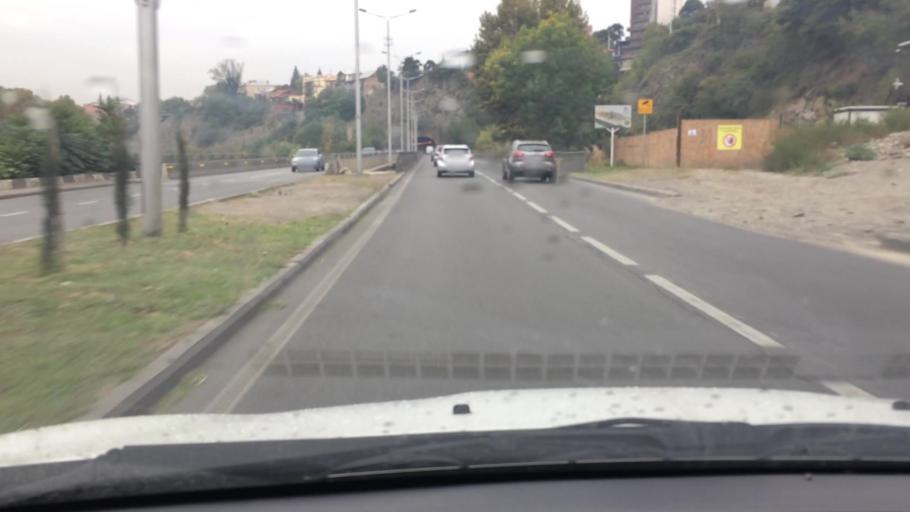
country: GE
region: T'bilisi
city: Tbilisi
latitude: 41.6862
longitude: 44.8228
